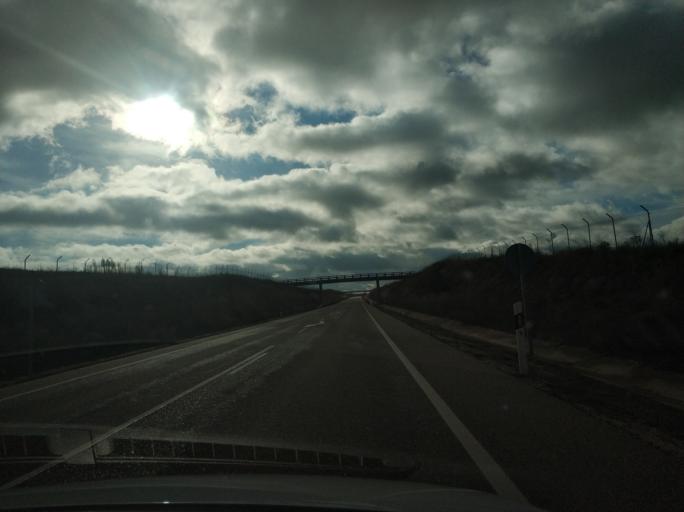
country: ES
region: Castille and Leon
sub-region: Provincia de Segovia
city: Ayllon
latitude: 41.4258
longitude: -3.3904
